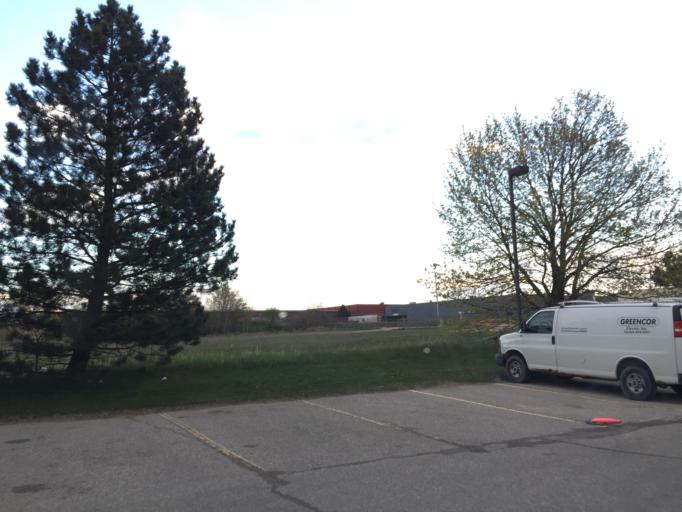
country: CA
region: Ontario
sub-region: Wellington County
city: Guelph
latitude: 43.5349
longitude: -80.3048
